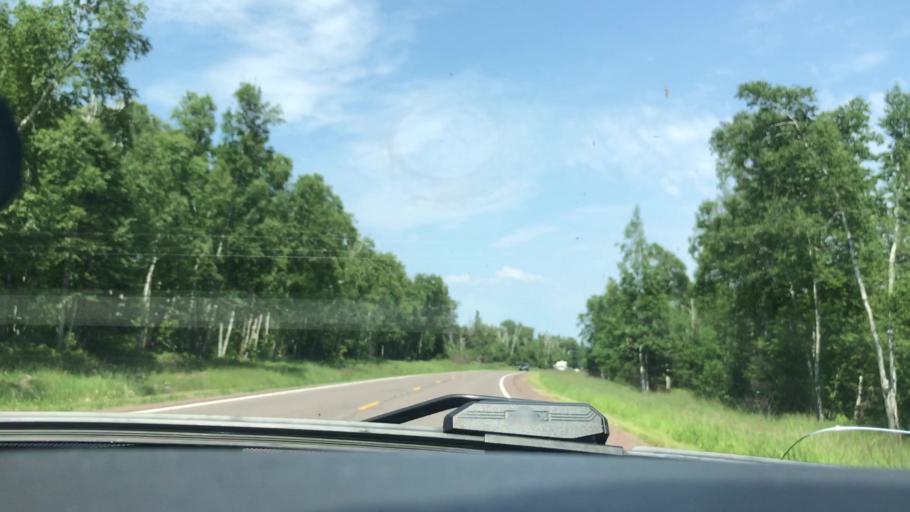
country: US
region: Minnesota
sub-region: Lake County
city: Silver Bay
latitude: 47.4992
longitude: -90.9690
